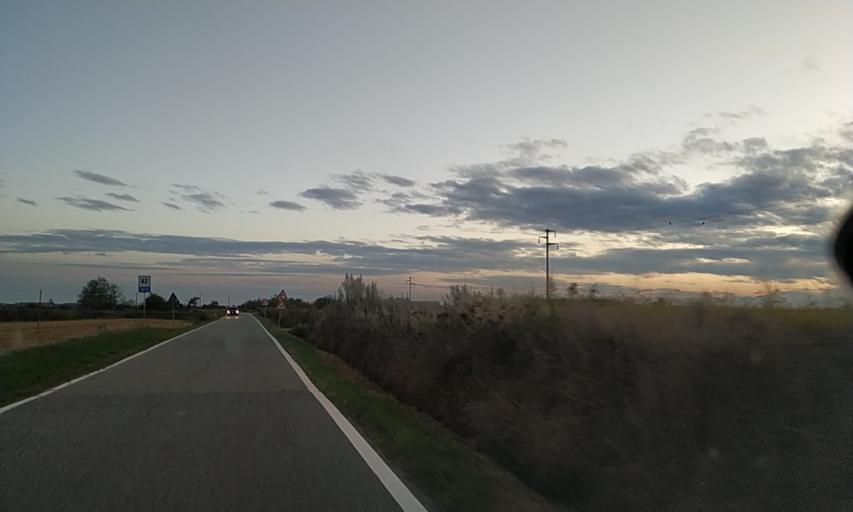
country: IT
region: Piedmont
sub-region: Provincia di Vercelli
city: San Giacomo Vercellese
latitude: 45.5075
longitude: 8.2912
